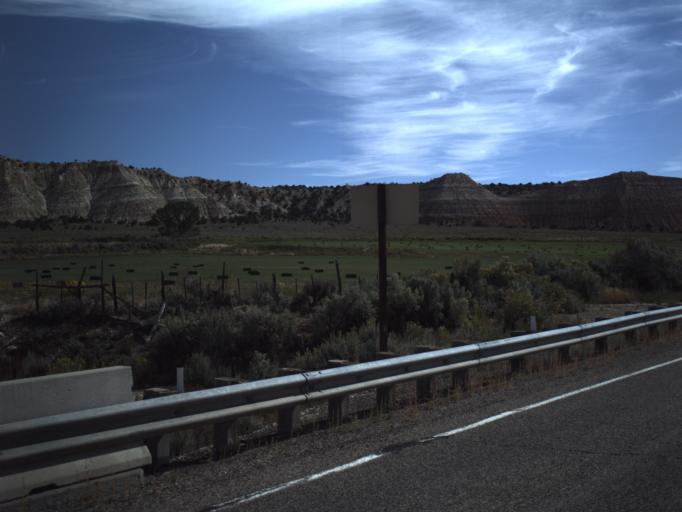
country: US
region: Utah
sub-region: Garfield County
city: Panguitch
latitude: 37.5675
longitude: -112.0512
